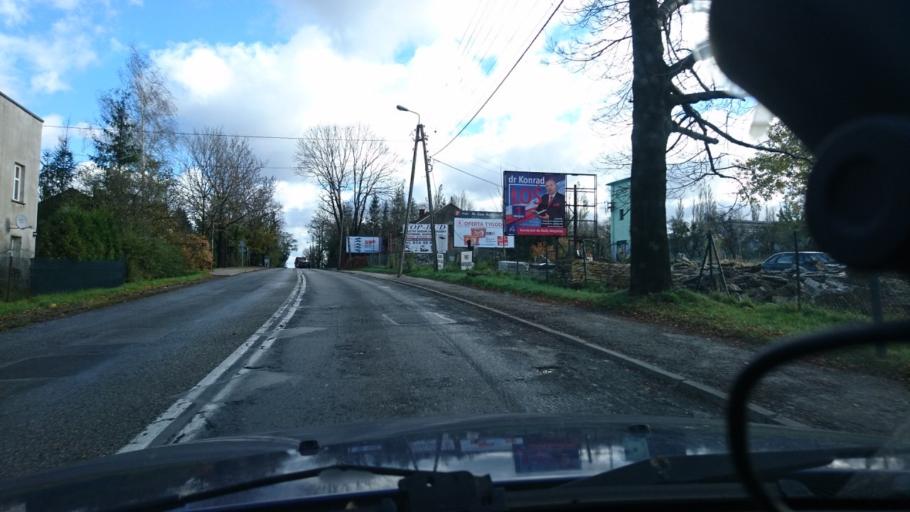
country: PL
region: Silesian Voivodeship
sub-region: Powiat bielski
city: Jaworze
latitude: 49.8087
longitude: 18.9955
